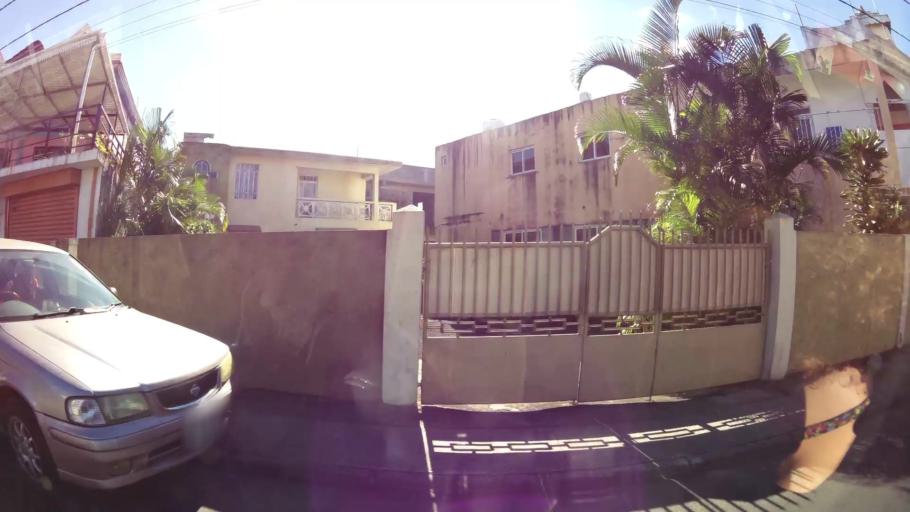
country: MU
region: Plaines Wilhems
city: Quatre Bornes
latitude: -20.2721
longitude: 57.4724
